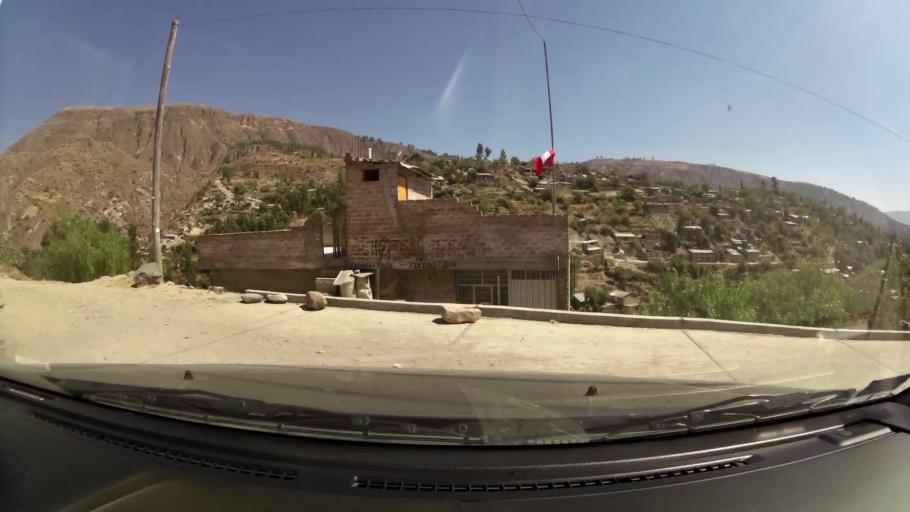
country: PE
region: Ayacucho
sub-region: Provincia de Huamanga
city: Carmen Alto
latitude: -13.1788
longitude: -74.2283
